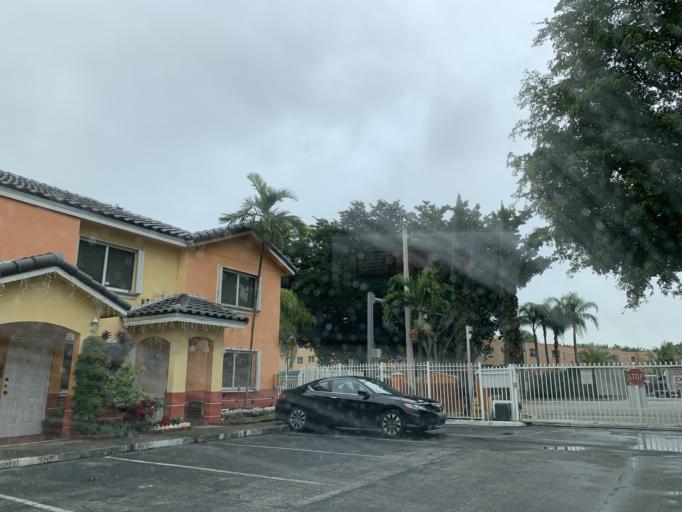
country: US
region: Florida
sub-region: Miami-Dade County
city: Kendall West
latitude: 25.6924
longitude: -80.4373
